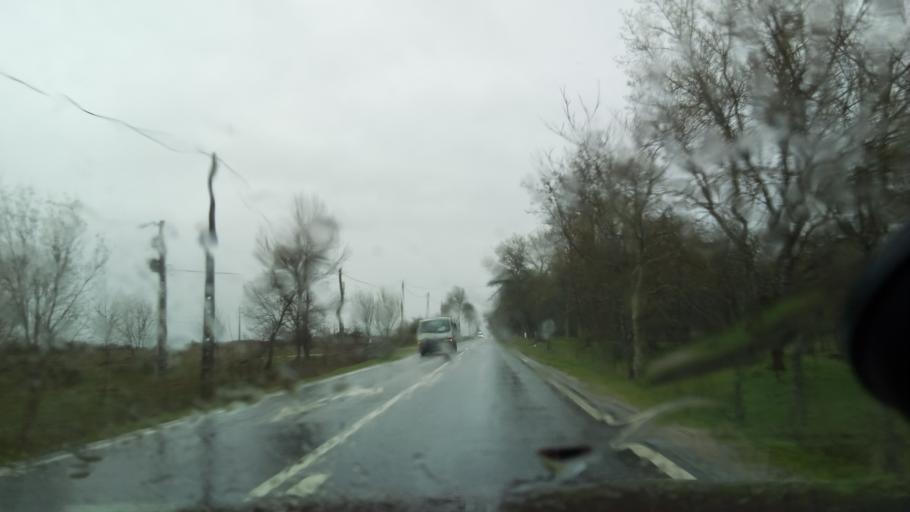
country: PT
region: Guarda
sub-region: Fornos de Algodres
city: Fornos de Algodres
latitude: 40.5361
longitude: -7.5485
